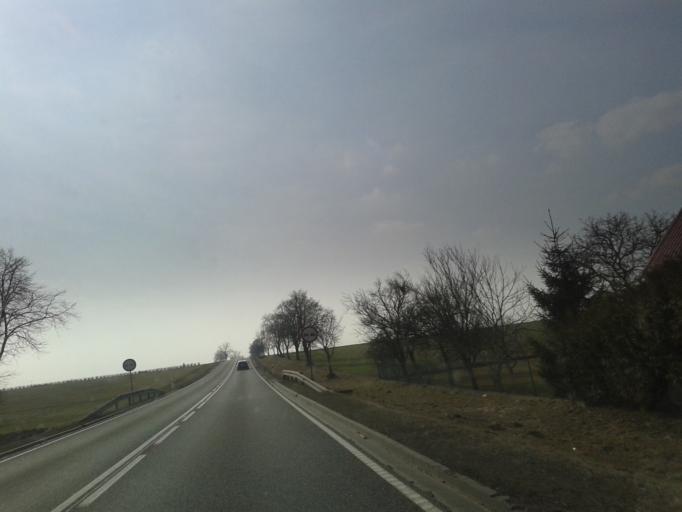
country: PL
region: Pomeranian Voivodeship
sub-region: Powiat czluchowski
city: Debrzno
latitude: 53.6053
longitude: 17.1477
